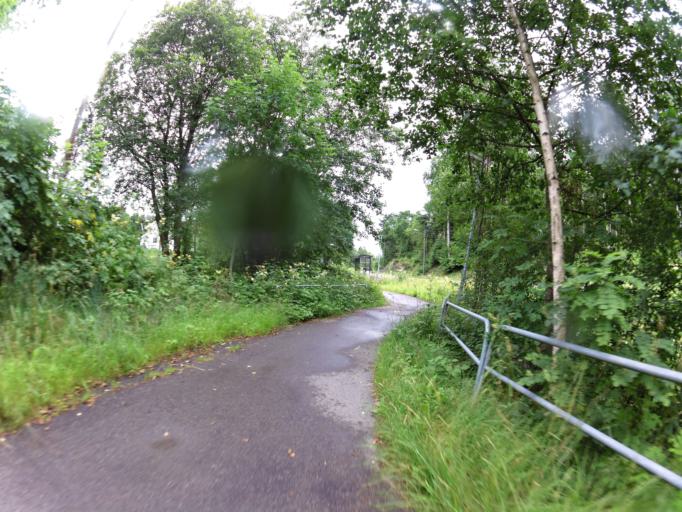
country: NO
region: Ostfold
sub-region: Moss
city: Moss
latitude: 59.4680
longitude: 10.6901
